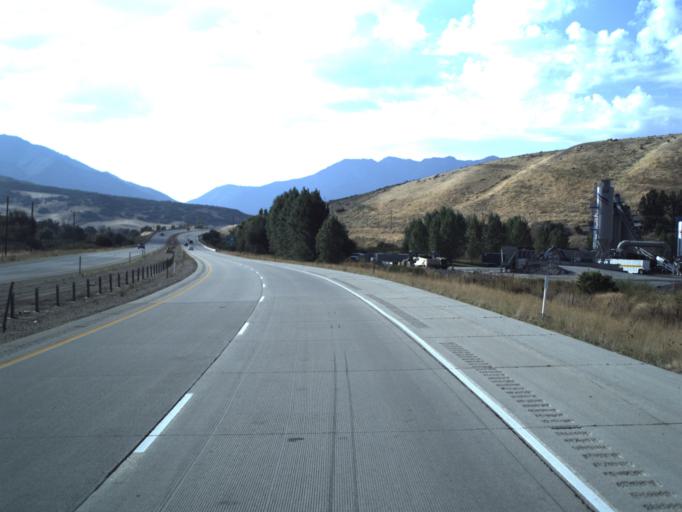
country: US
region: Utah
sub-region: Morgan County
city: Mountain Green
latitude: 41.1102
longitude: -111.7515
